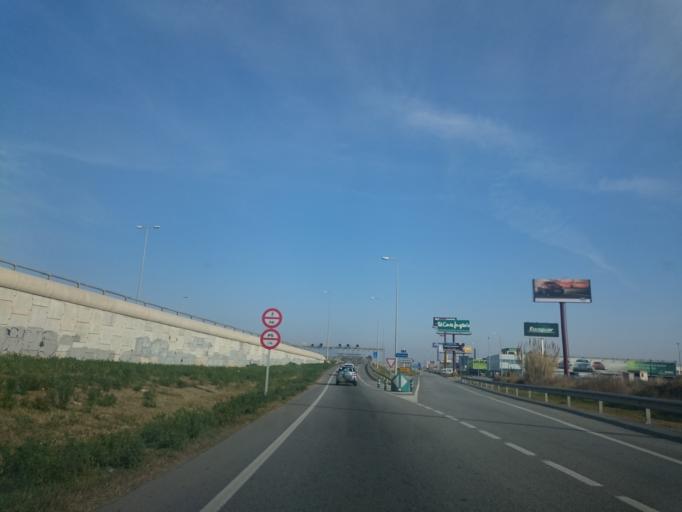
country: ES
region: Catalonia
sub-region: Provincia de Barcelona
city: El Prat de Llobregat
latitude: 41.3059
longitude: 2.0623
